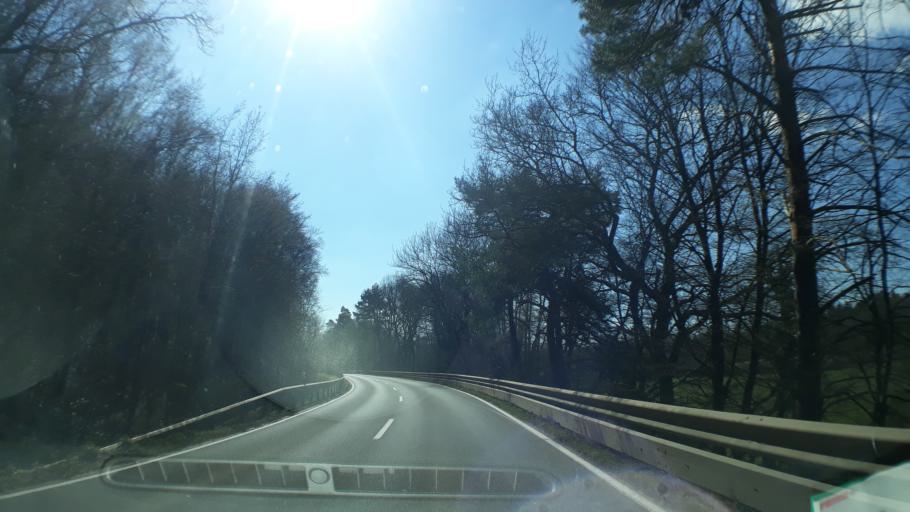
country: DE
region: North Rhine-Westphalia
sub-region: Regierungsbezirk Koln
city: Mechernich
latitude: 50.5982
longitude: 6.6801
